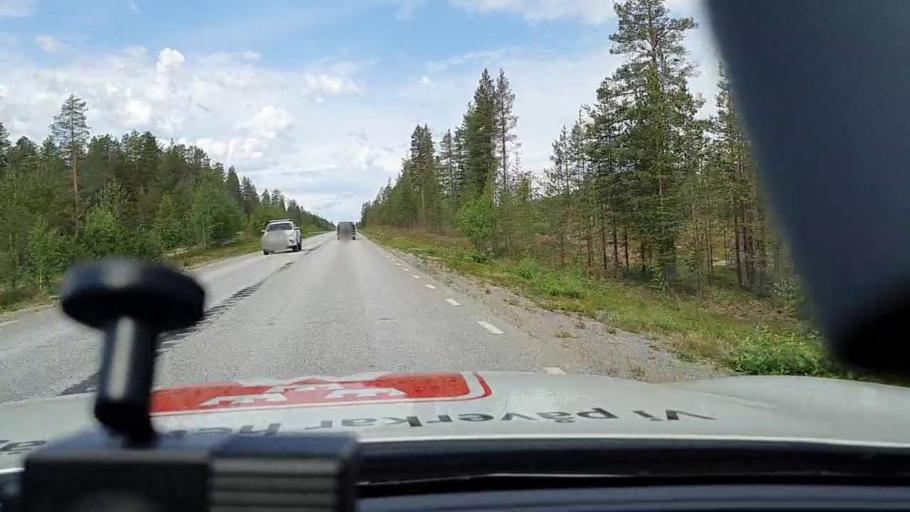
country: SE
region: Norrbotten
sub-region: Jokkmokks Kommun
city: Jokkmokk
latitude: 66.5223
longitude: 20.2085
